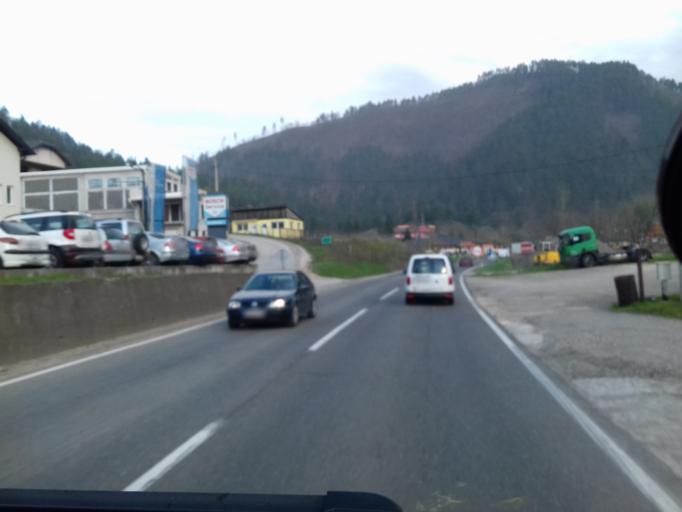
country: BA
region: Federation of Bosnia and Herzegovina
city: Maglaj
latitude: 44.5752
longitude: 18.0979
